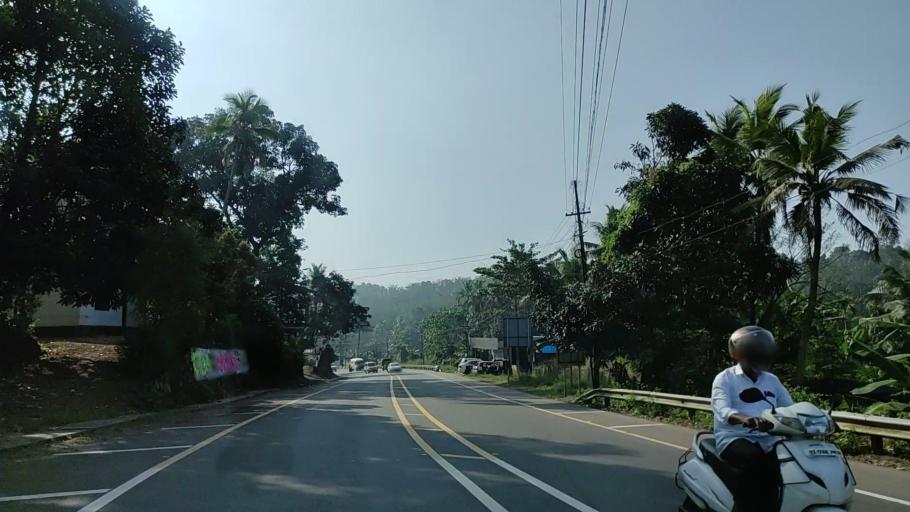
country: IN
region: Kerala
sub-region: Kollam
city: Punalur
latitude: 8.9621
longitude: 76.8374
